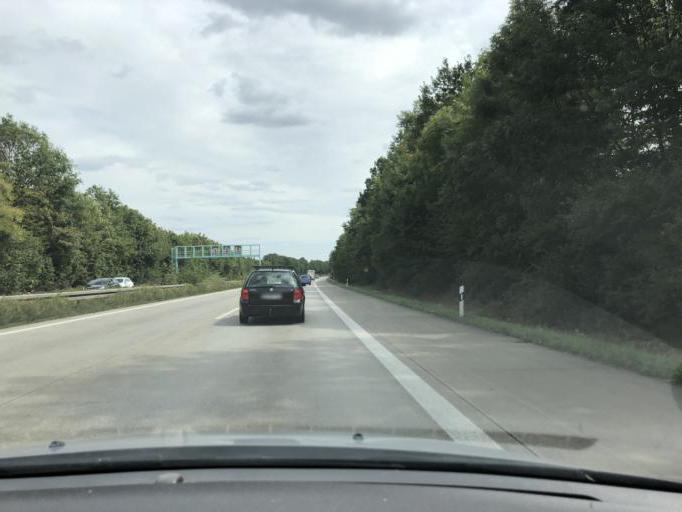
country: DE
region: North Rhine-Westphalia
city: Wickede
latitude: 51.5330
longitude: 7.8289
